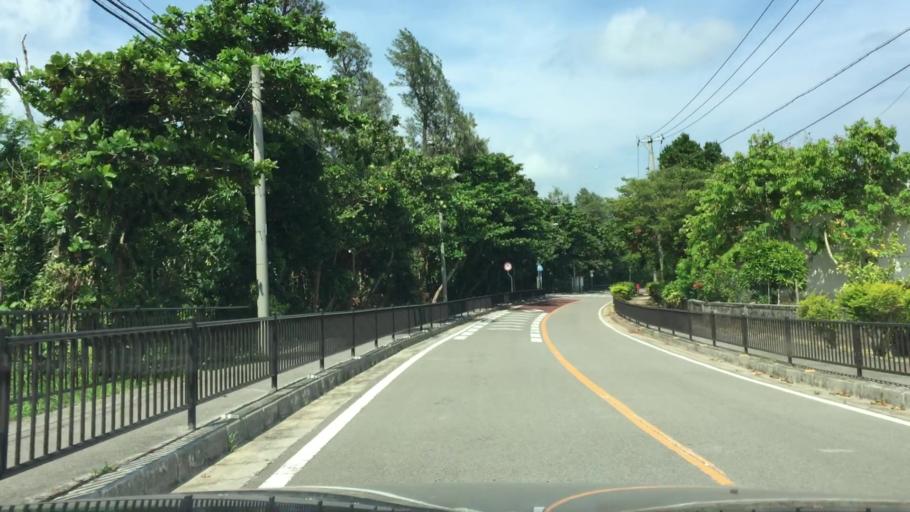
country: JP
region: Okinawa
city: Ishigaki
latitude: 24.4976
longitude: 124.2357
